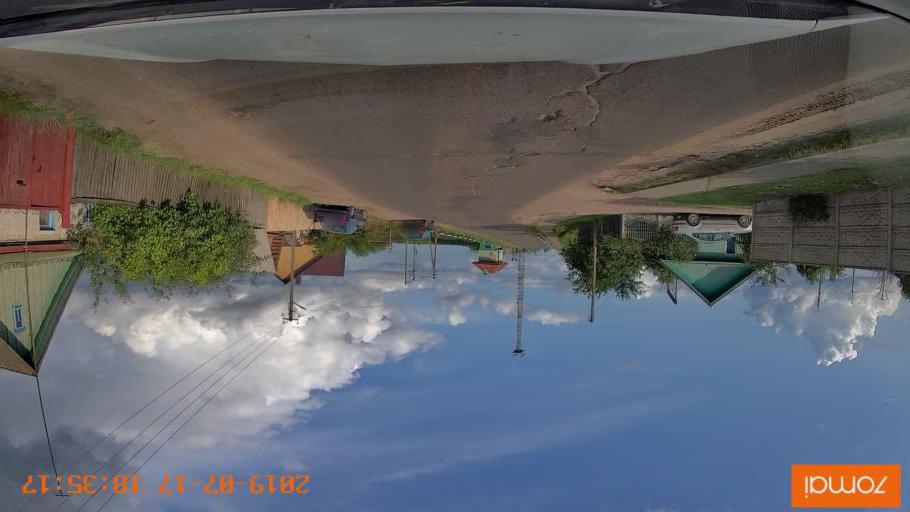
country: BY
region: Mogilev
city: Asipovichy
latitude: 53.2916
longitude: 28.6571
